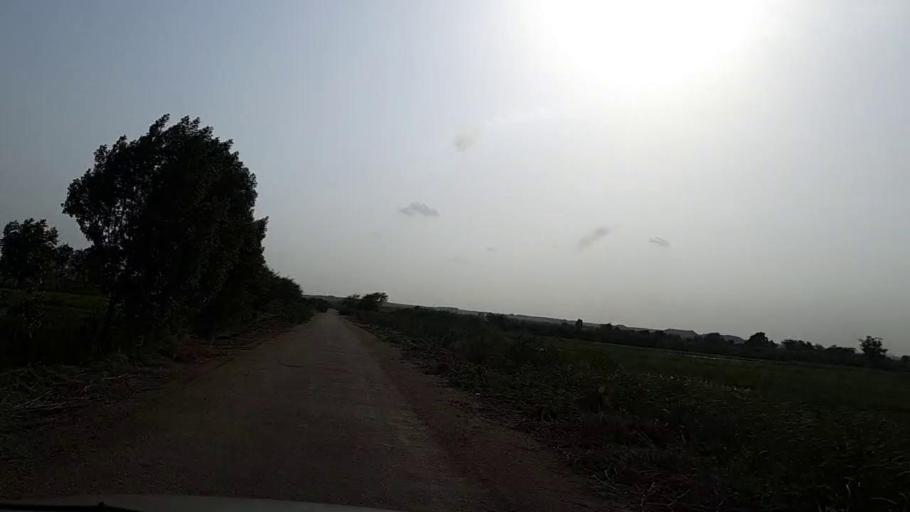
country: PK
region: Sindh
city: Kotri
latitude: 25.1856
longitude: 68.2540
